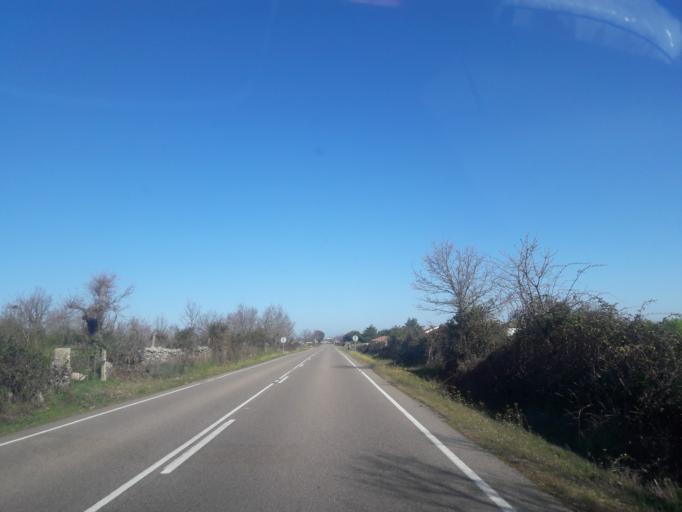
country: ES
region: Castille and Leon
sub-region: Provincia de Salamanca
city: Valderrodrigo
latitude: 41.0657
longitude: -6.5123
